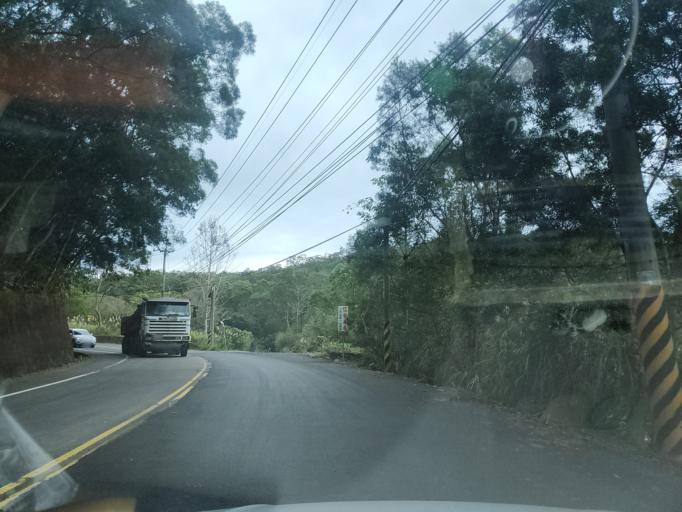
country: TW
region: Taiwan
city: Fengyuan
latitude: 24.3731
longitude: 120.7699
